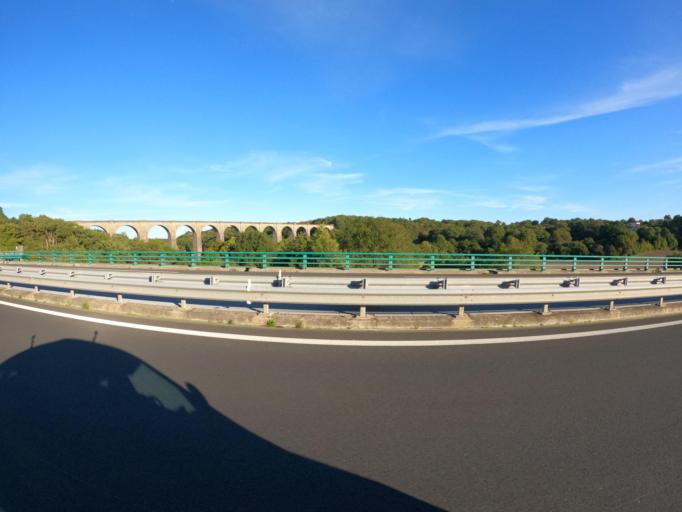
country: FR
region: Pays de la Loire
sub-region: Departement de la Vendee
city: Saint-Laurent-sur-Sevre
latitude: 46.9673
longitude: -0.9201
